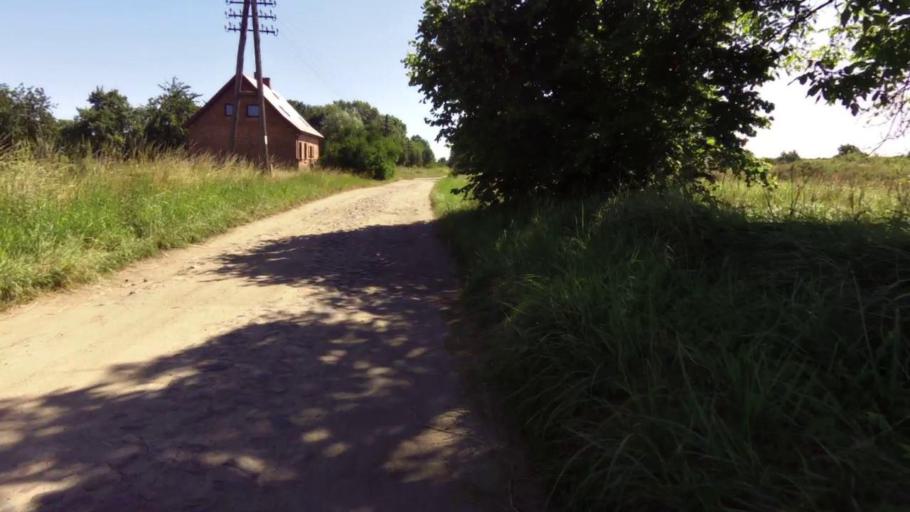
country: PL
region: West Pomeranian Voivodeship
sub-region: Powiat drawski
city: Wierzchowo
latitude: 53.5249
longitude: 16.1444
